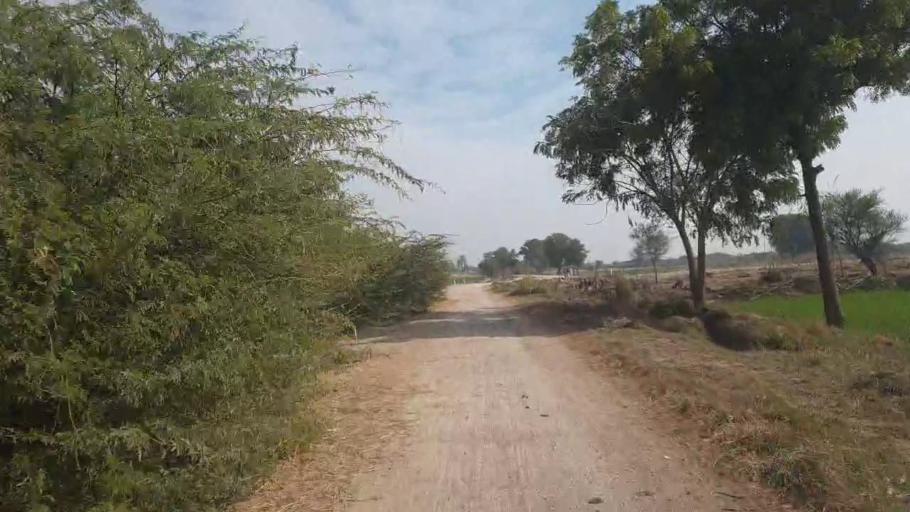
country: PK
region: Sindh
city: Nawabshah
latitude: 26.1139
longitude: 68.4897
